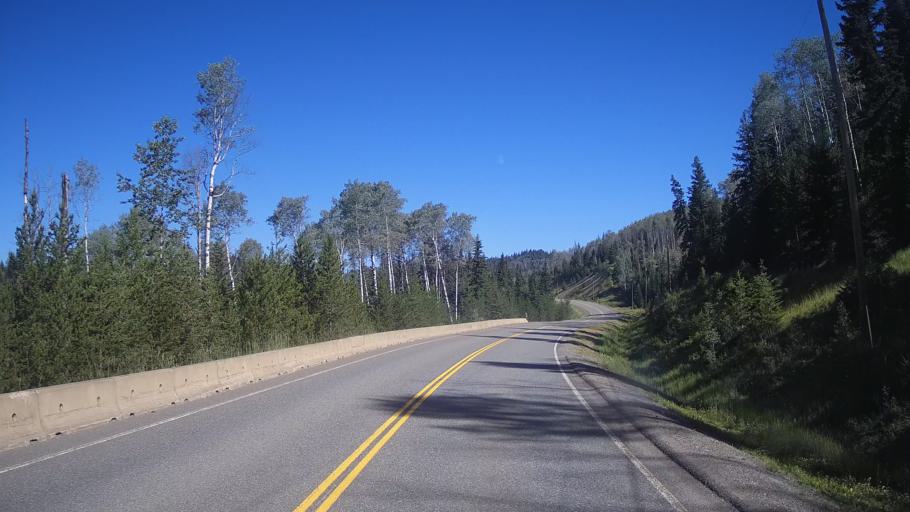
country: CA
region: British Columbia
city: Kamloops
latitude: 51.4793
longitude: -120.5622
